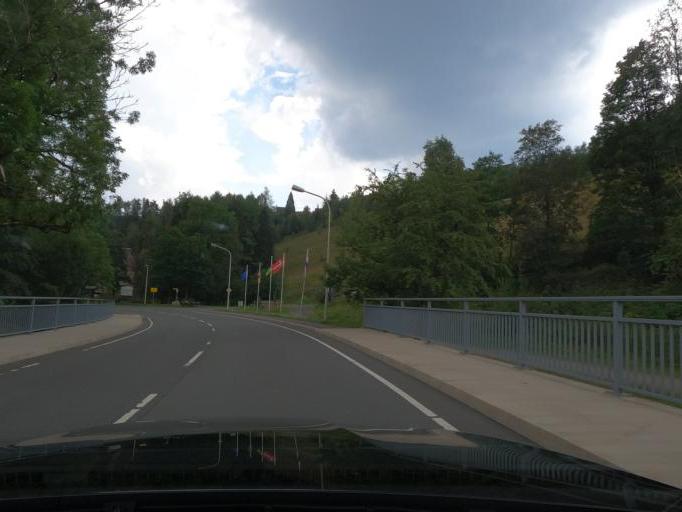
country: DE
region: Lower Saxony
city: Wildemann
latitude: 51.8280
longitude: 10.2736
